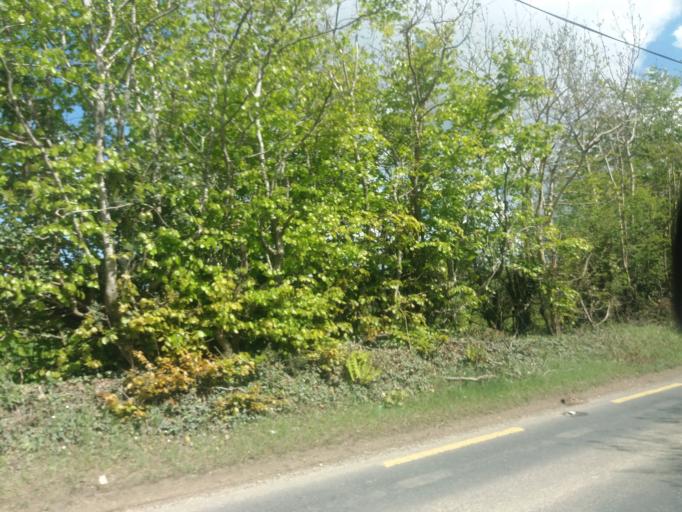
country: IE
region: Leinster
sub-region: Loch Garman
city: Loch Garman
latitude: 52.2850
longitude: -6.6294
